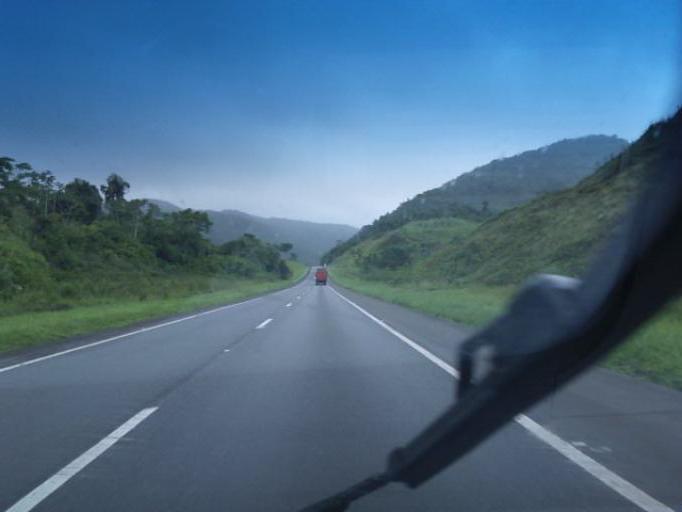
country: BR
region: Sao Paulo
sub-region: Cajati
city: Cajati
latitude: -24.9084
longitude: -48.2510
